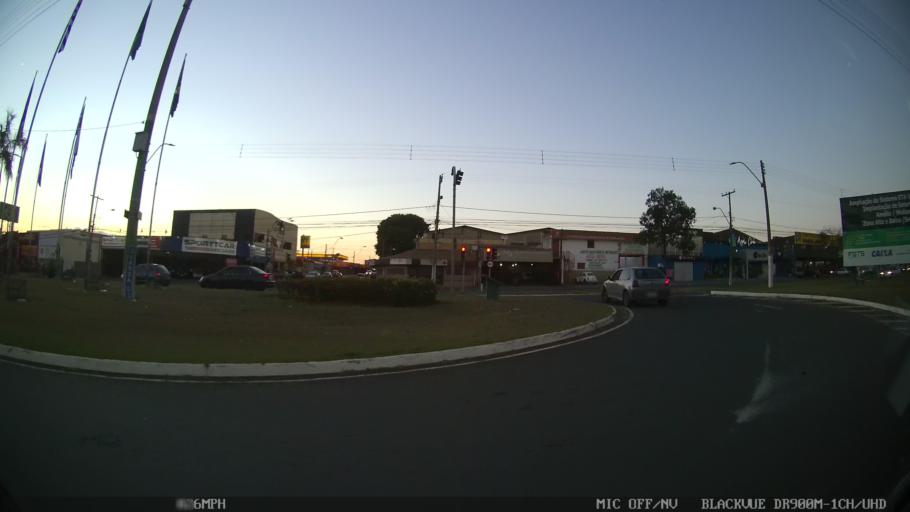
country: BR
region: Sao Paulo
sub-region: Americana
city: Americana
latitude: -22.7477
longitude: -47.3694
